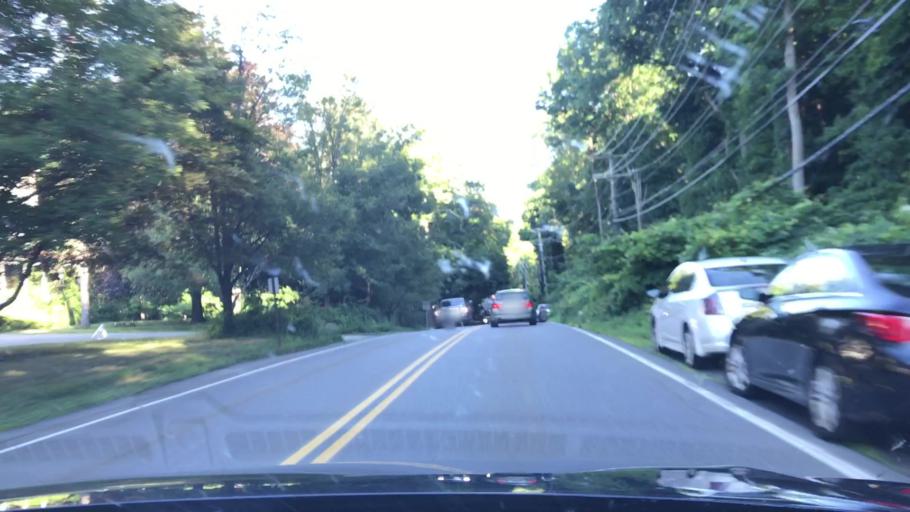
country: US
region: New York
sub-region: Westchester County
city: Heritage Hills
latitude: 41.3523
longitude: -73.6675
